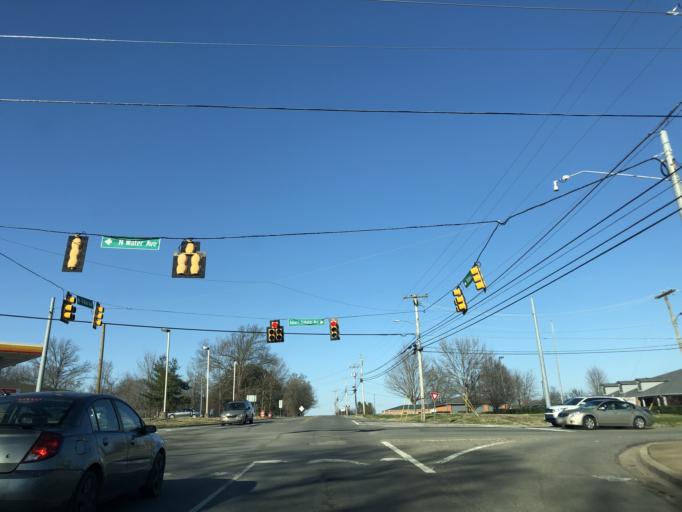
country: US
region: Tennessee
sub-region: Sumner County
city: Gallatin
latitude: 36.4043
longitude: -86.4451
